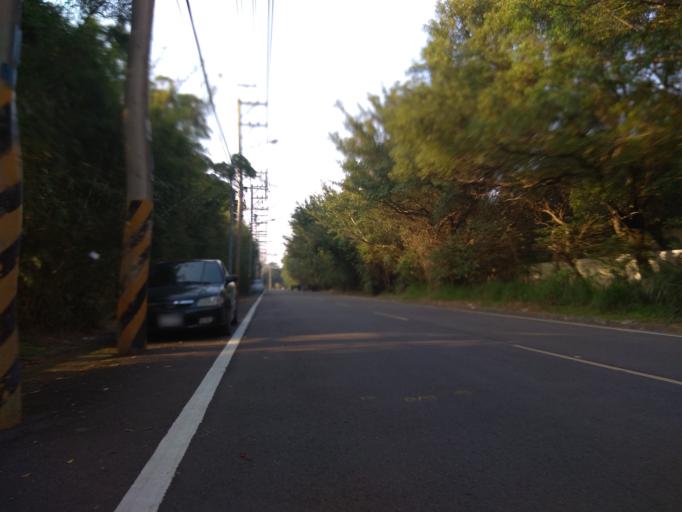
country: TW
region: Taiwan
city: Daxi
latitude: 24.9279
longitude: 121.1805
